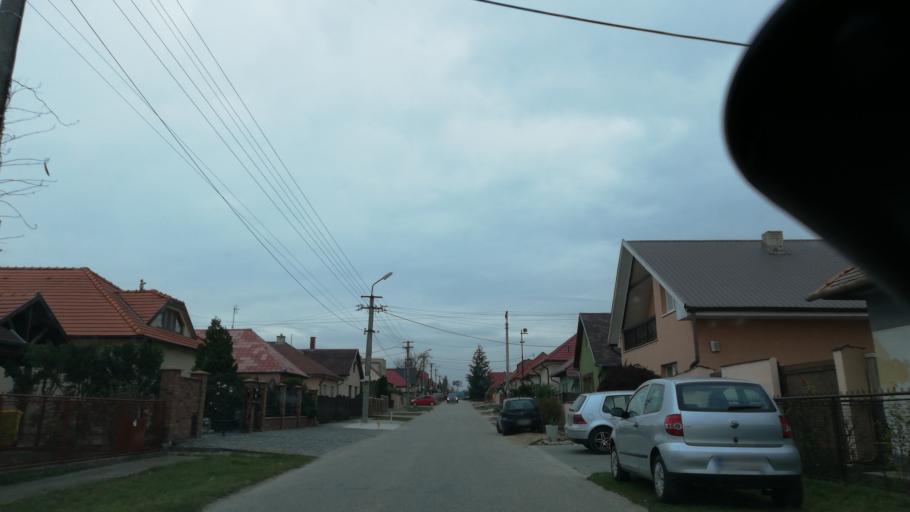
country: SK
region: Nitriansky
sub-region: Okres Nitra
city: Nitra
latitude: 48.3165
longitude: 17.9895
